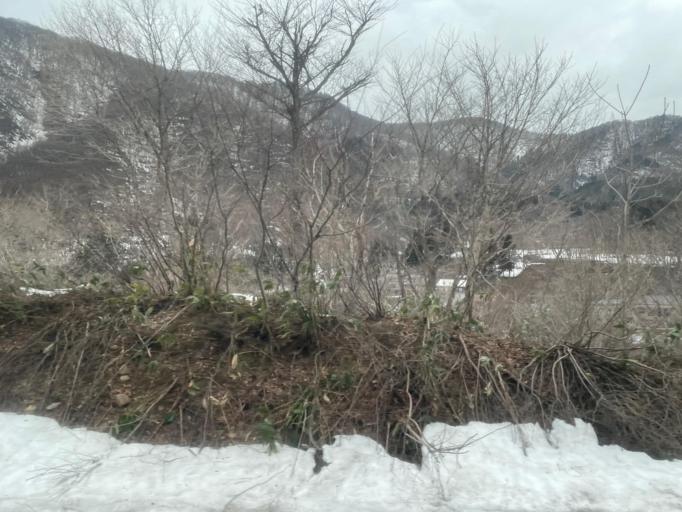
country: JP
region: Gunma
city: Numata
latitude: 36.7898
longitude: 138.9820
